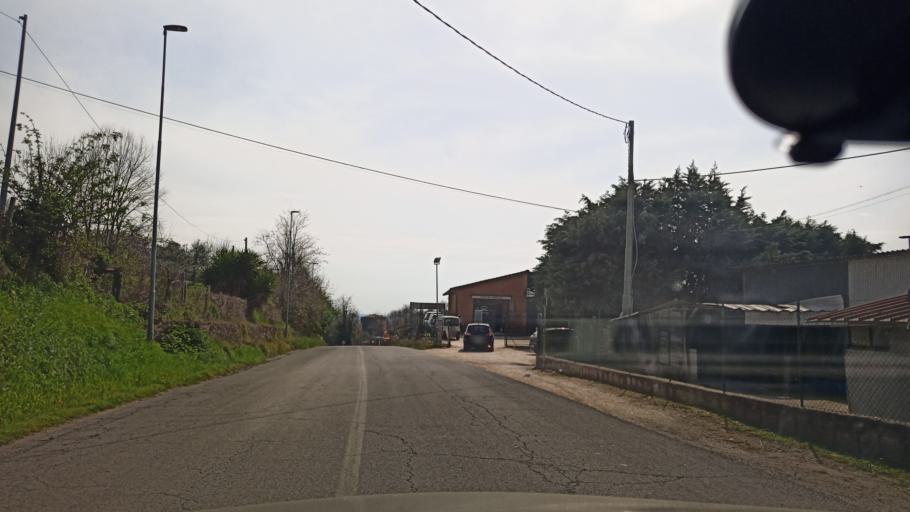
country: IT
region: Latium
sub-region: Provincia di Rieti
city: Cantalupo in Sabina
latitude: 42.3051
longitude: 12.6454
